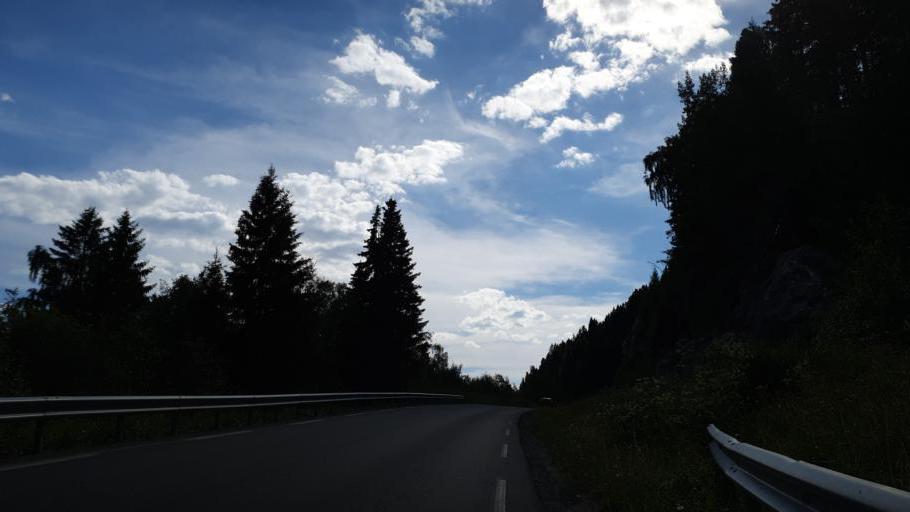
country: NO
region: Nord-Trondelag
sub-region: Leksvik
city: Leksvik
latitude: 63.6187
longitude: 10.5223
